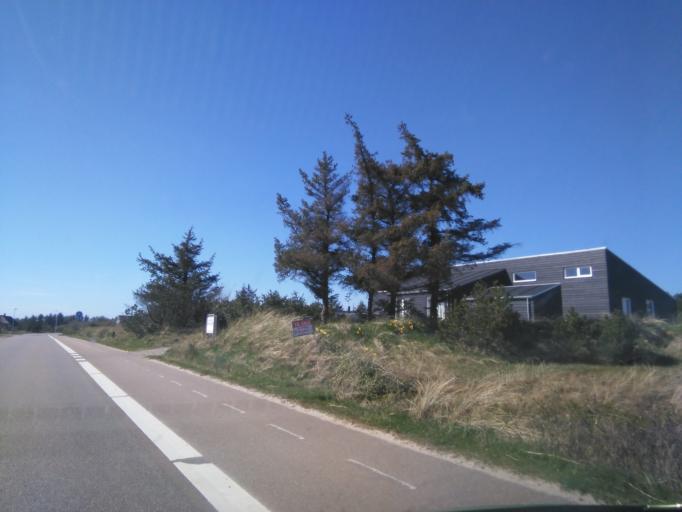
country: DK
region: South Denmark
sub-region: Varde Kommune
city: Oksbol
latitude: 55.5494
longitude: 8.1511
